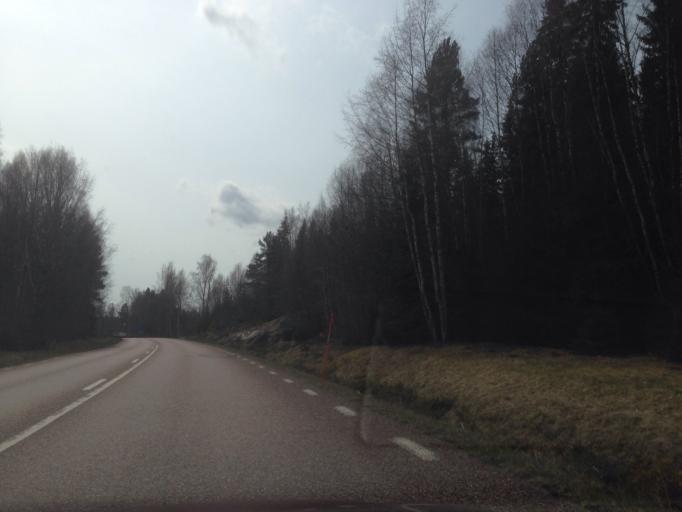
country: SE
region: Dalarna
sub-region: Ludvika Kommun
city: Grangesberg
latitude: 60.2134
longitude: 14.9574
